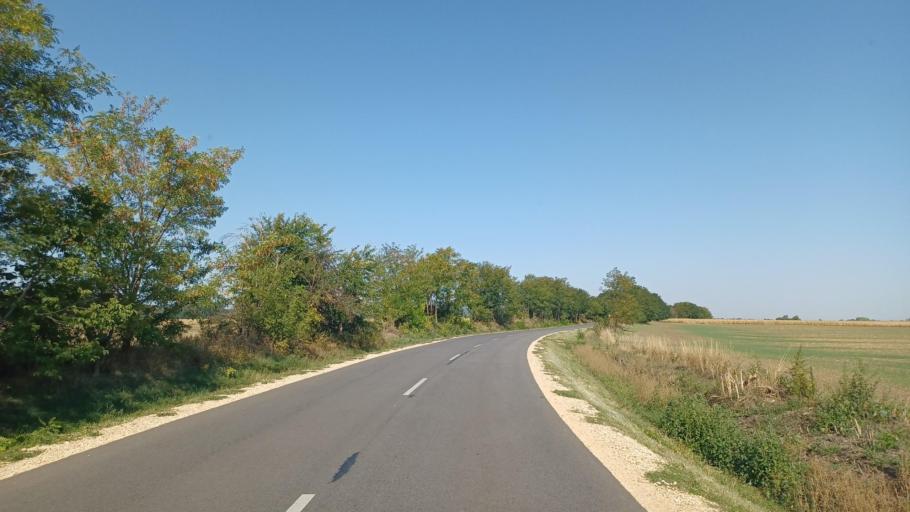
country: HU
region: Tolna
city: Nemetker
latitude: 46.6983
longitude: 18.7904
